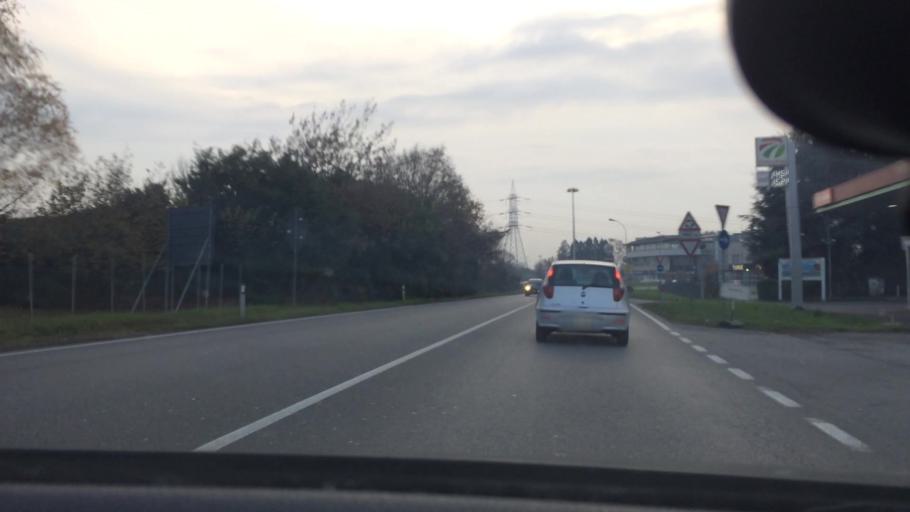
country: IT
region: Lombardy
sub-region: Provincia di Monza e Brianza
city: Varedo
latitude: 45.5985
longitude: 9.1680
